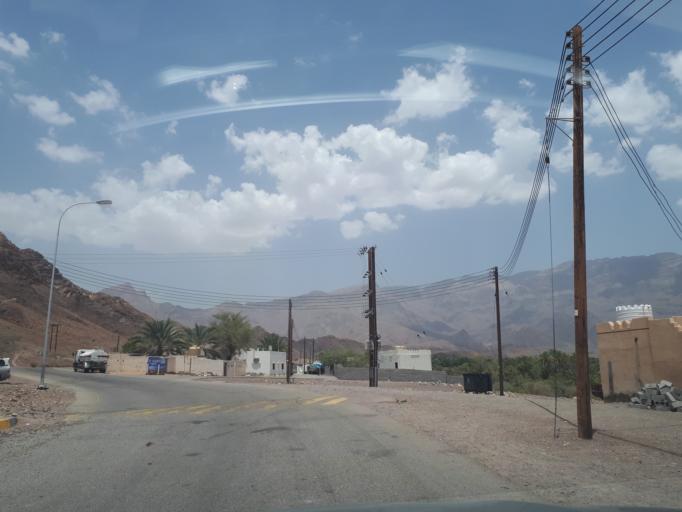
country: OM
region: Ash Sharqiyah
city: Badiyah
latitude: 22.4694
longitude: 59.1058
